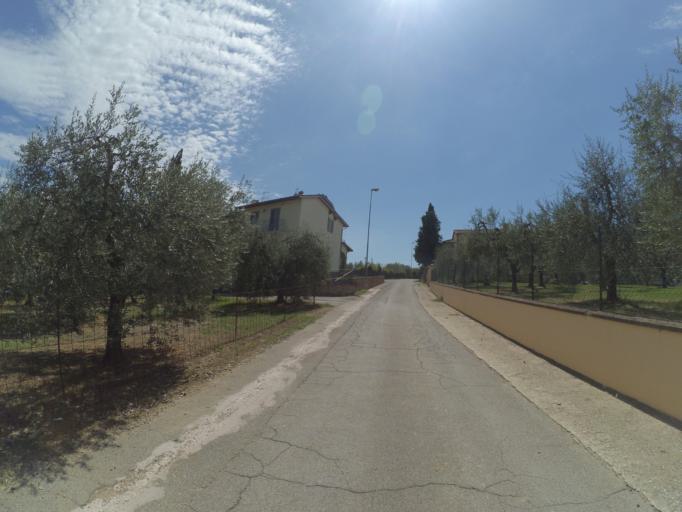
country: IT
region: Tuscany
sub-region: Province of Arezzo
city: Castiglion Fibocchi
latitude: 43.5314
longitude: 11.7666
